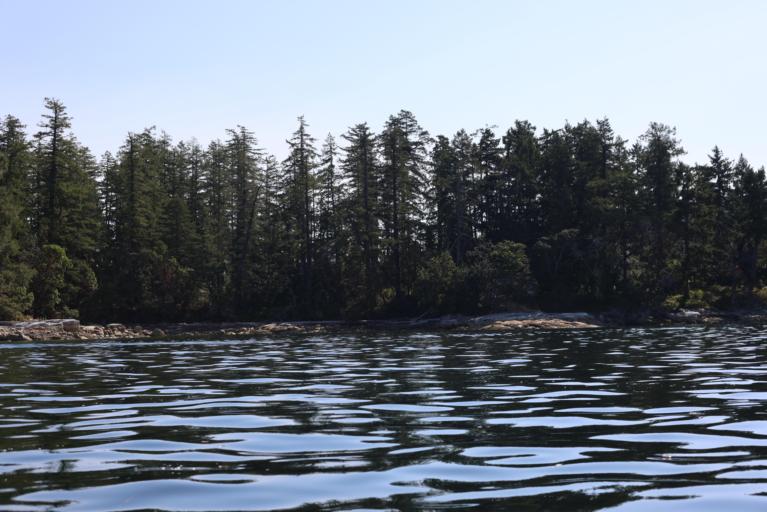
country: CA
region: British Columbia
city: North Saanich
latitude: 48.6277
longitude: -123.4814
